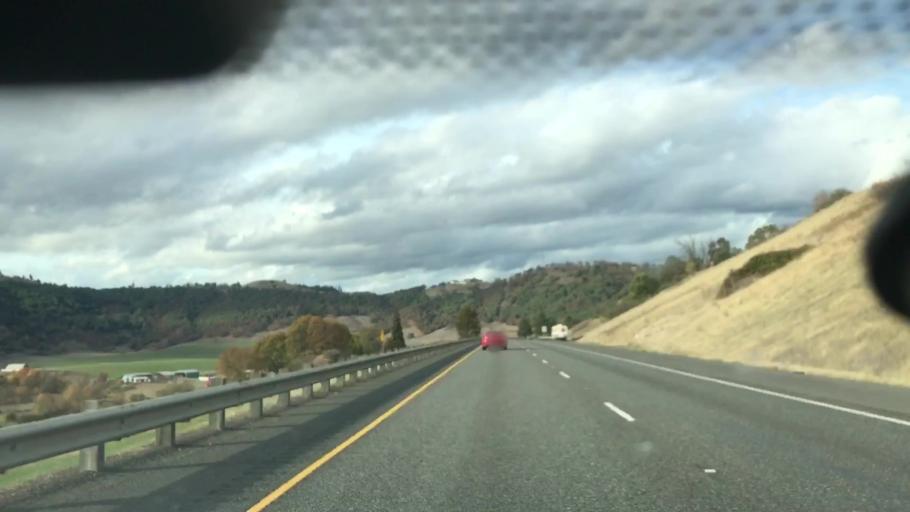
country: US
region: Oregon
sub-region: Douglas County
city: Winston
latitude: 43.0867
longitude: -123.3667
